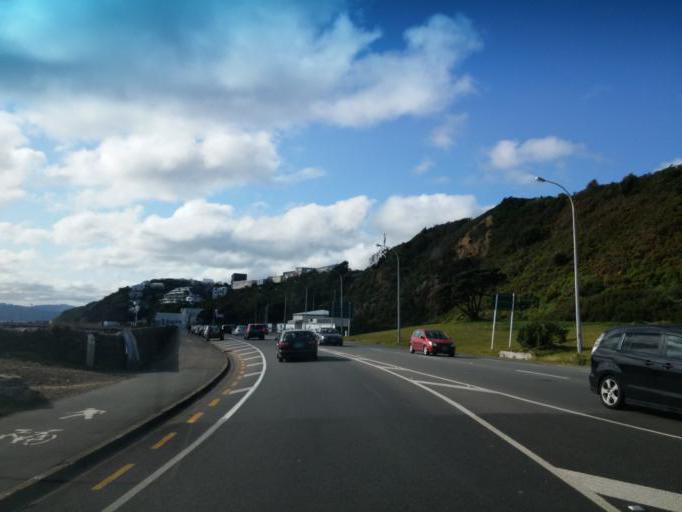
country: NZ
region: Wellington
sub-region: Wellington City
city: Wellington
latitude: -41.3162
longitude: 174.8097
